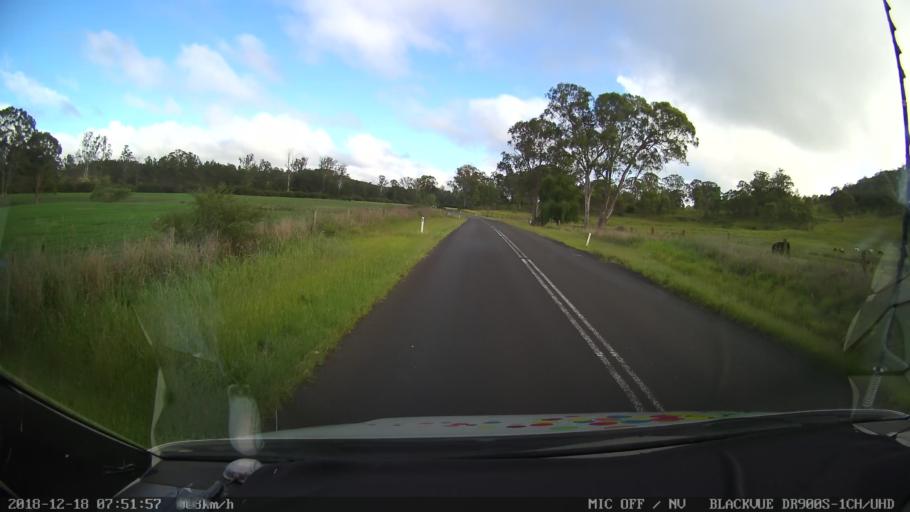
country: AU
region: New South Wales
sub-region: Kyogle
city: Kyogle
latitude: -28.4333
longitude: 152.5809
